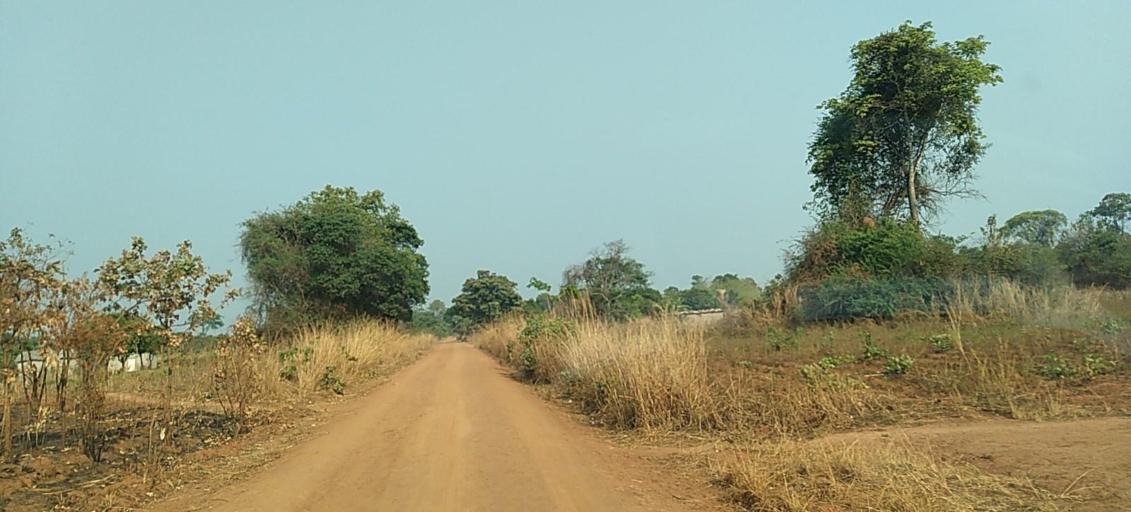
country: ZM
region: Copperbelt
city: Chingola
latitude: -12.8561
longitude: 27.5607
